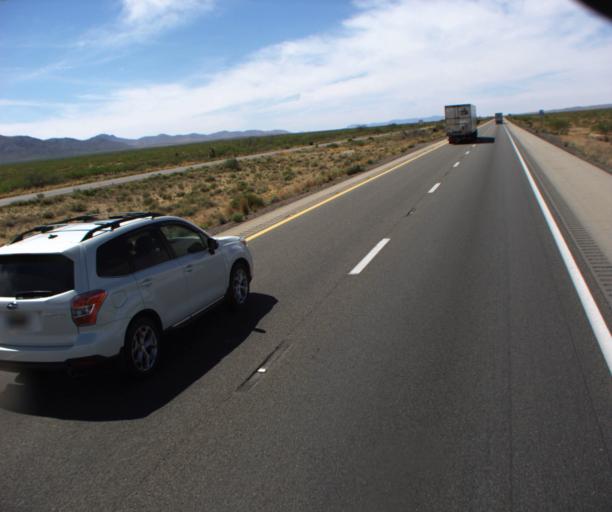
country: US
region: Arizona
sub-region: Cochise County
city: Willcox
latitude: 32.3341
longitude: -109.5269
